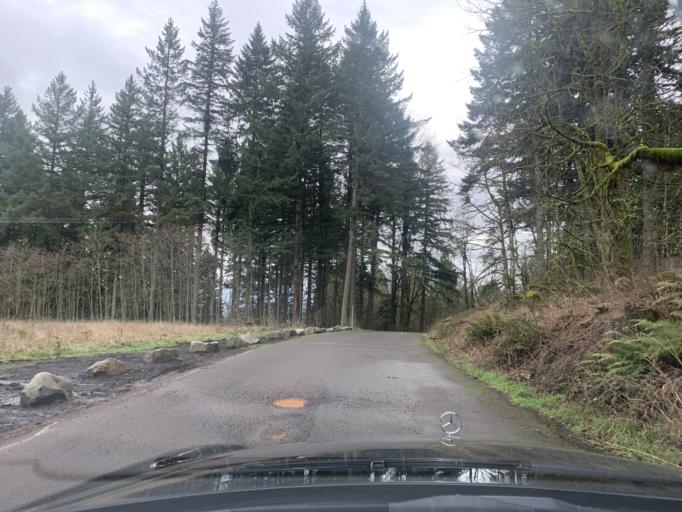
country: US
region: Oregon
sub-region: Clackamas County
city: Happy Valley
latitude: 45.4462
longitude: -122.5073
